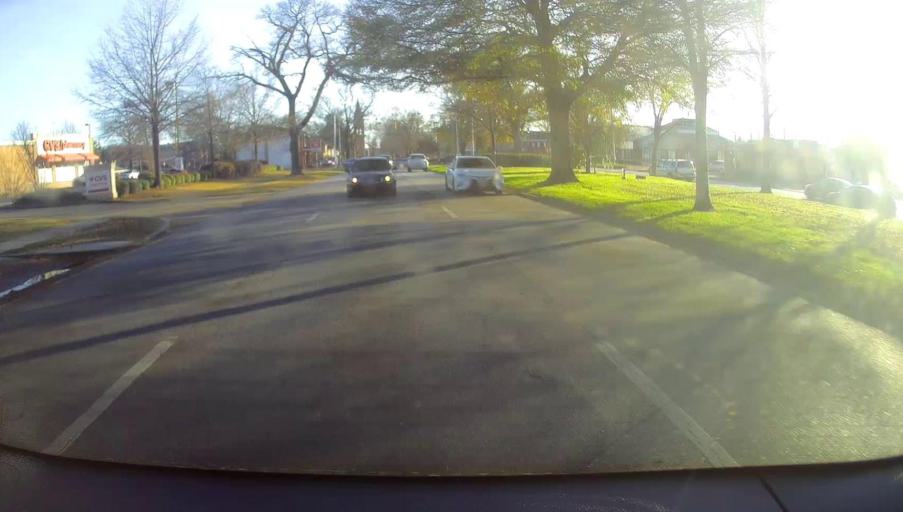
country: US
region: Alabama
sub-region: Calhoun County
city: Anniston
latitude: 33.6633
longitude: -85.8266
